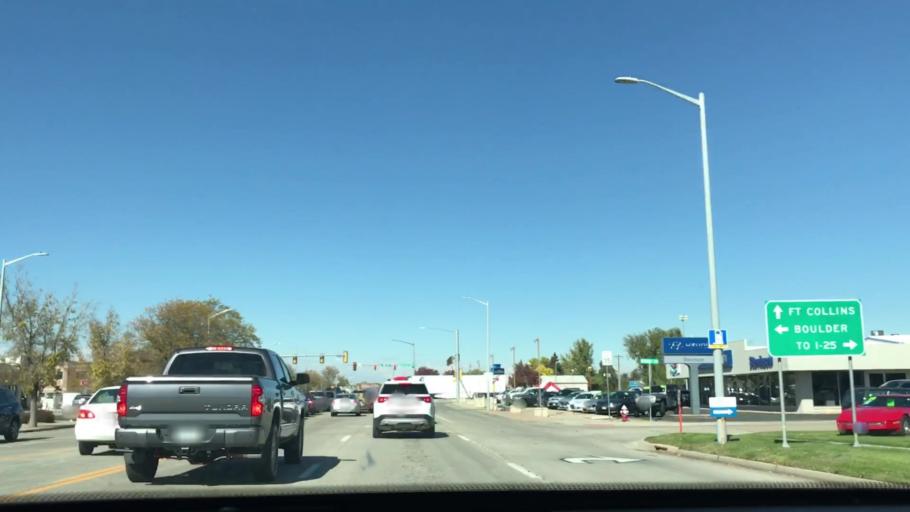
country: US
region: Colorado
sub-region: Boulder County
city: Longmont
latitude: 40.1512
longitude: -105.1025
